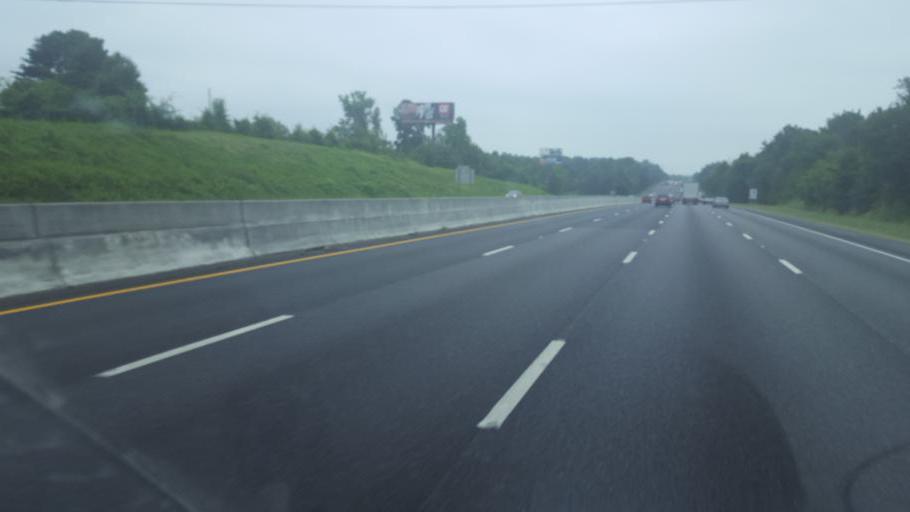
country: US
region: South Carolina
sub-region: York County
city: Fort Mill
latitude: 35.0432
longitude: -80.9595
